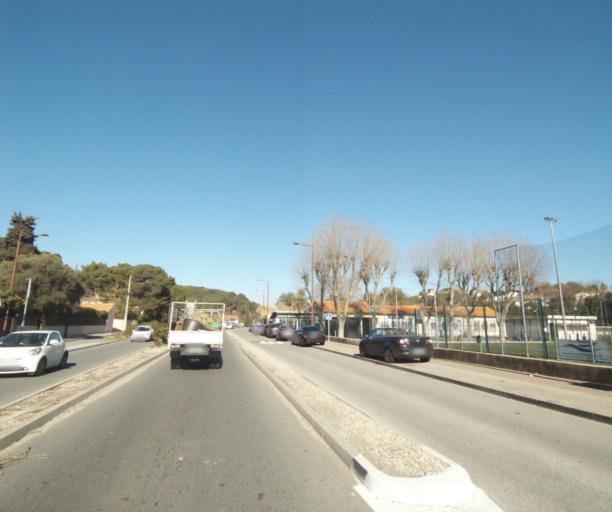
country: FR
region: Provence-Alpes-Cote d'Azur
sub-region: Departement des Alpes-Maritimes
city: Vallauris
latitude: 43.5816
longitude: 7.0897
